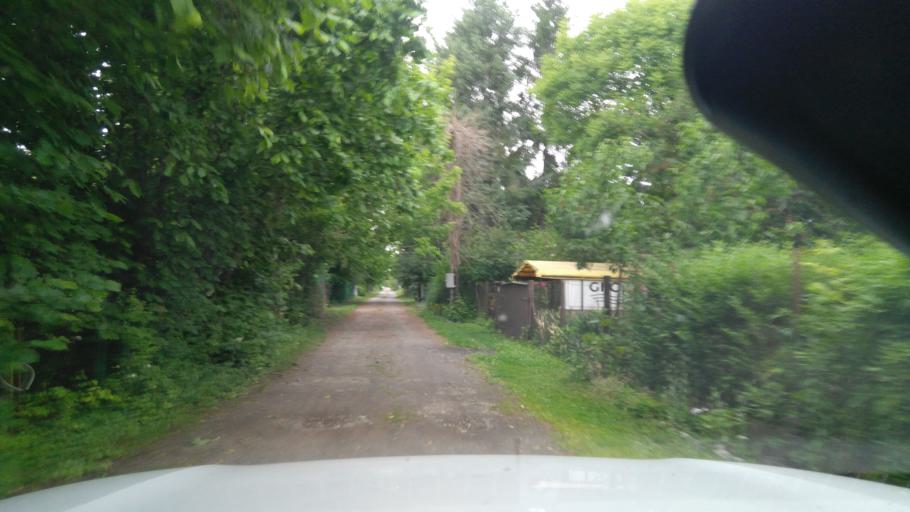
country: HU
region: Bekes
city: Doboz
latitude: 46.6730
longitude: 21.1903
